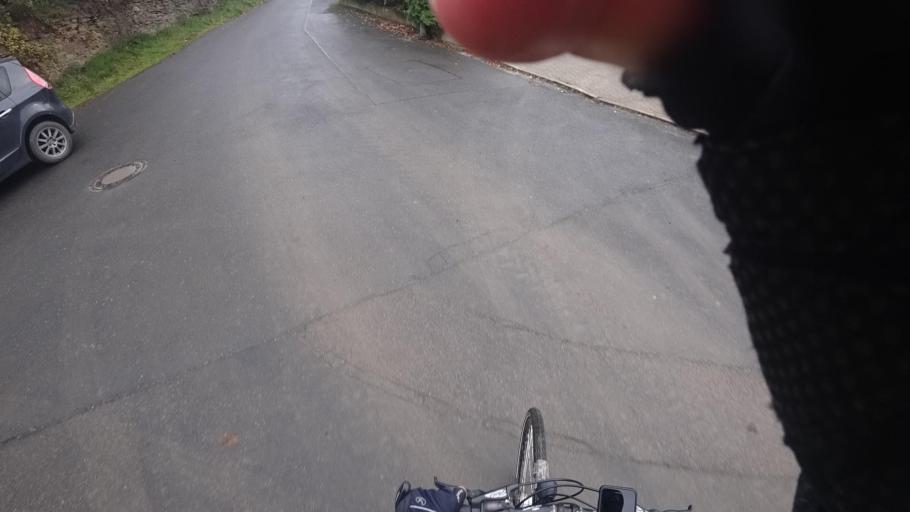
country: DE
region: Rheinland-Pfalz
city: Dernau
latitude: 50.5272
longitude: 7.0427
